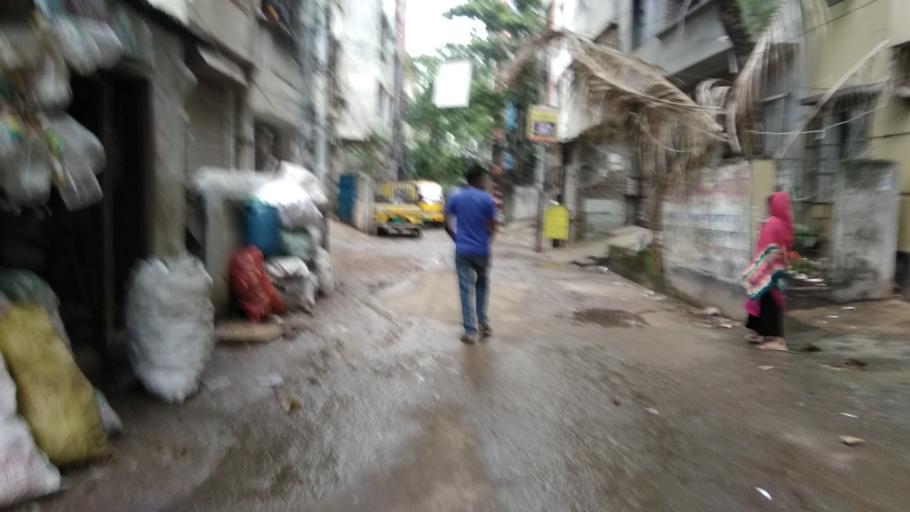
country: BD
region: Dhaka
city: Tungi
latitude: 23.8258
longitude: 90.3689
